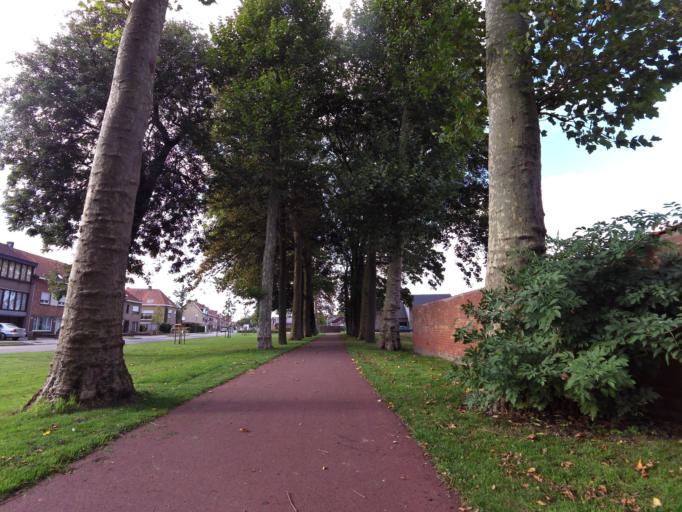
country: BE
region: Flanders
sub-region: Provincie West-Vlaanderen
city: Sint-Kruis
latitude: 51.2280
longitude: 3.2379
